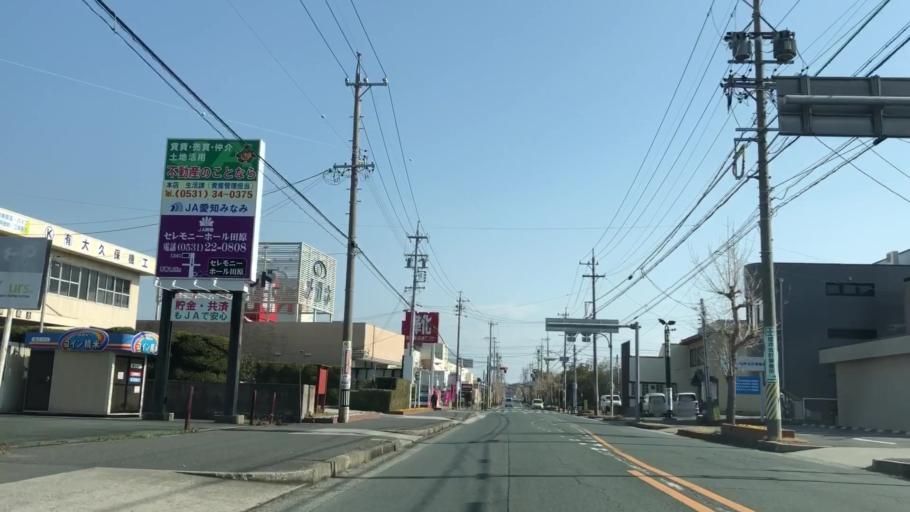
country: JP
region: Aichi
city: Tahara
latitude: 34.6736
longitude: 137.2721
